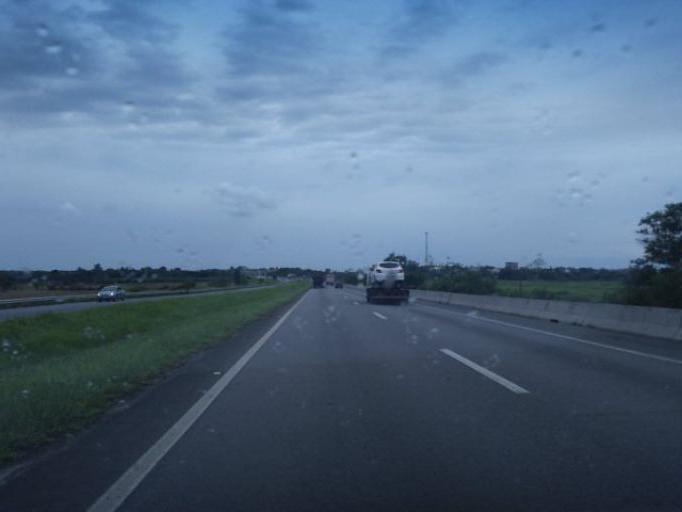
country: BR
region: Sao Paulo
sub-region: Registro
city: Registro
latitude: -24.4794
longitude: -47.8300
